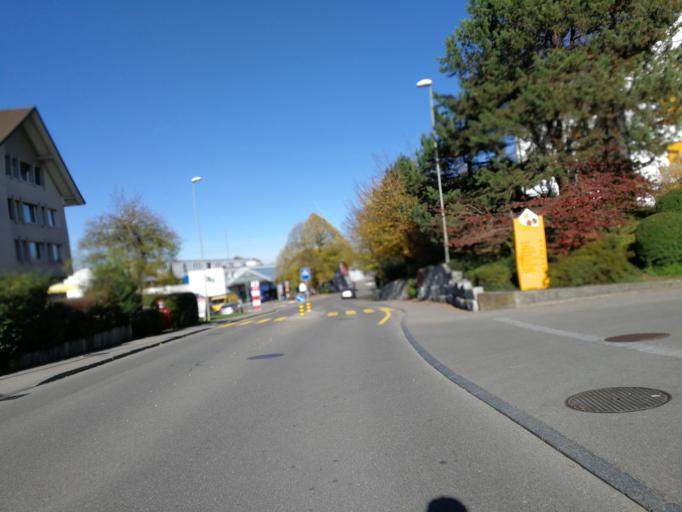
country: CH
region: Zurich
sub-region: Bezirk Hinwil
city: Binzikon
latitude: 47.2804
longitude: 8.7601
